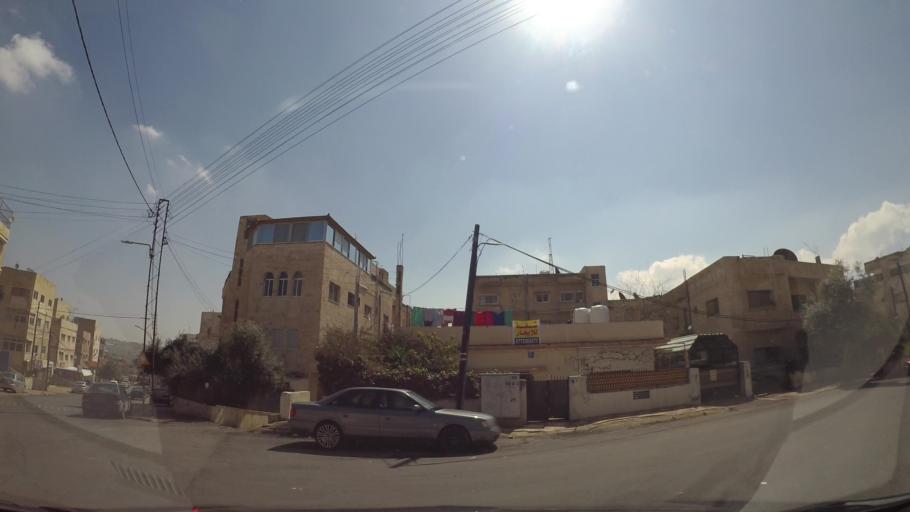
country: JO
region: Amman
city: Amman
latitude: 31.9762
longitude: 35.9888
